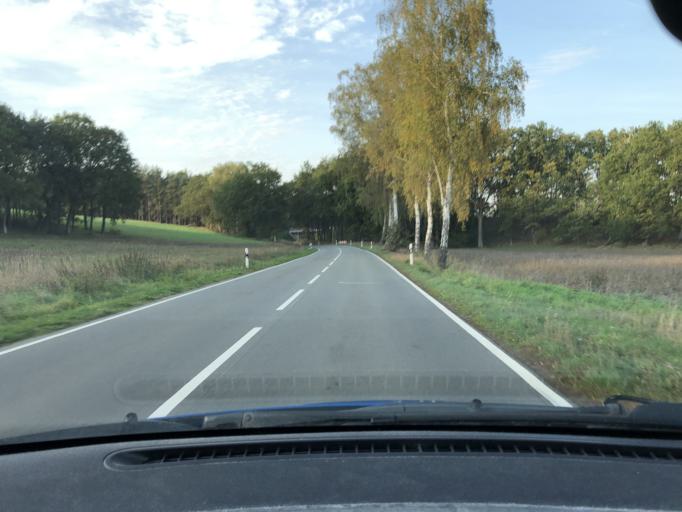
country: DE
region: Lower Saxony
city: Hitzacker
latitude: 53.1313
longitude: 11.0474
